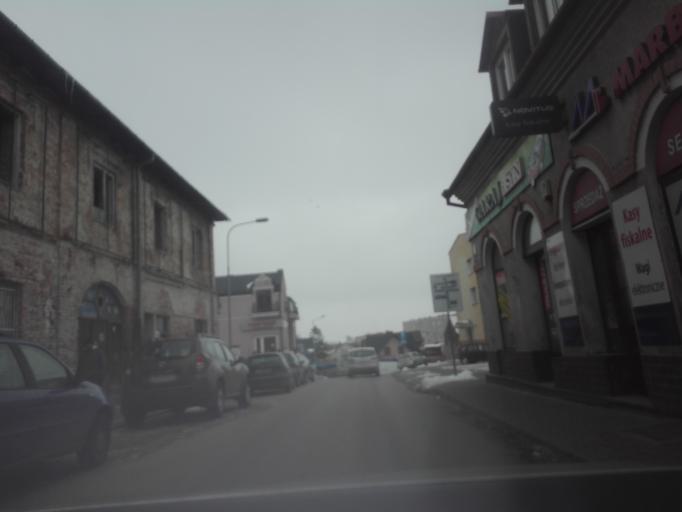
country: PL
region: Lublin Voivodeship
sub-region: Powiat hrubieszowski
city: Hrubieszow
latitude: 50.8060
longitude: 23.8917
